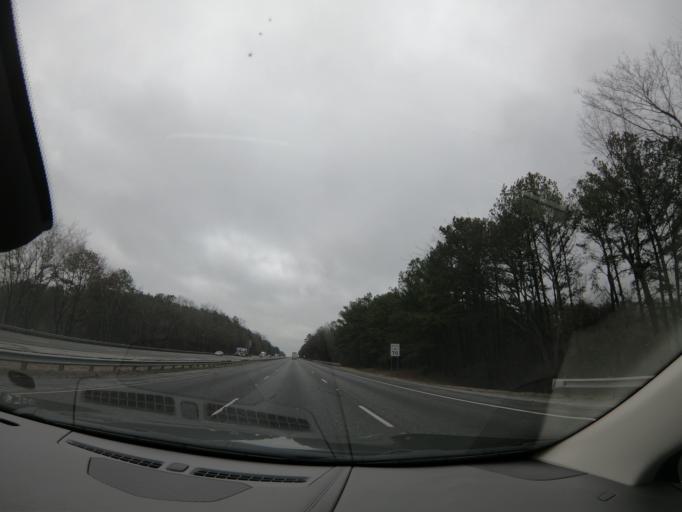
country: US
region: Georgia
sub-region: Gordon County
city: Calhoun
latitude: 34.5862
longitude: -84.9530
